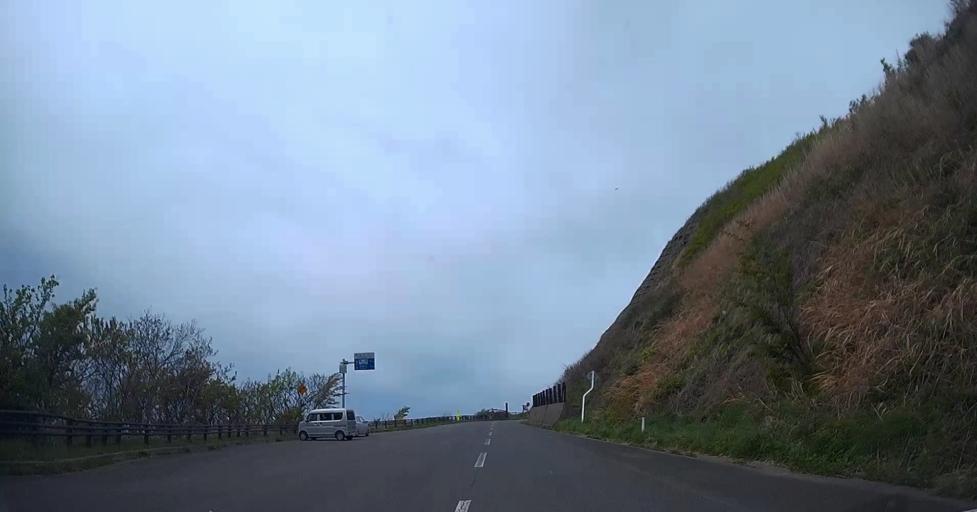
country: JP
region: Aomori
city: Shimokizukuri
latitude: 41.1954
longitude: 140.3352
